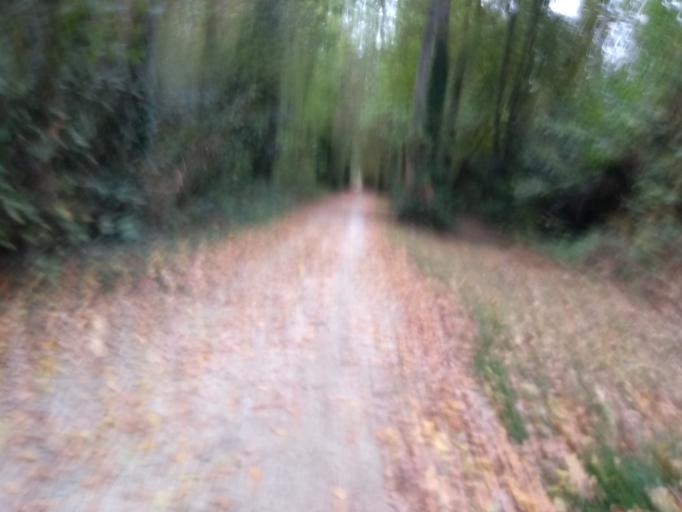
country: FR
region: Aquitaine
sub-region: Departement de la Gironde
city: Pessac
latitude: 44.7924
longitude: -0.6606
